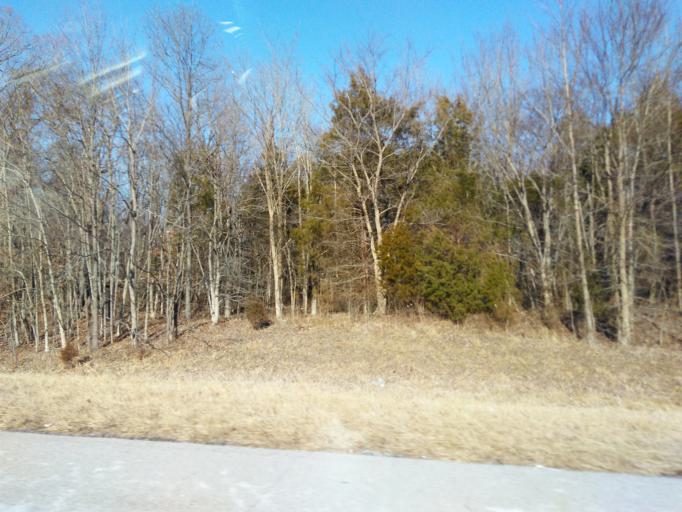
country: US
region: Illinois
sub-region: Johnson County
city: Vienna
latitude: 37.3914
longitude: -88.8381
